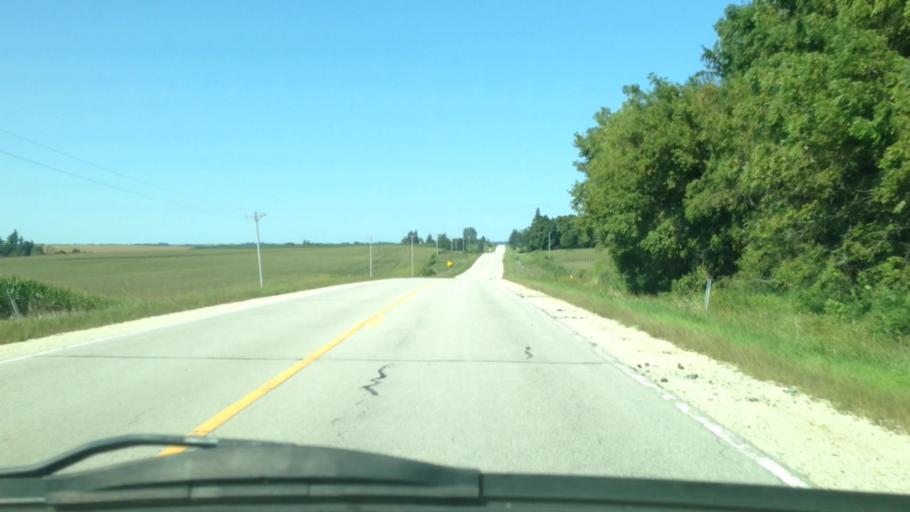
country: US
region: Minnesota
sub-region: Houston County
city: Spring Grove
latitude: 43.6084
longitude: -91.7903
